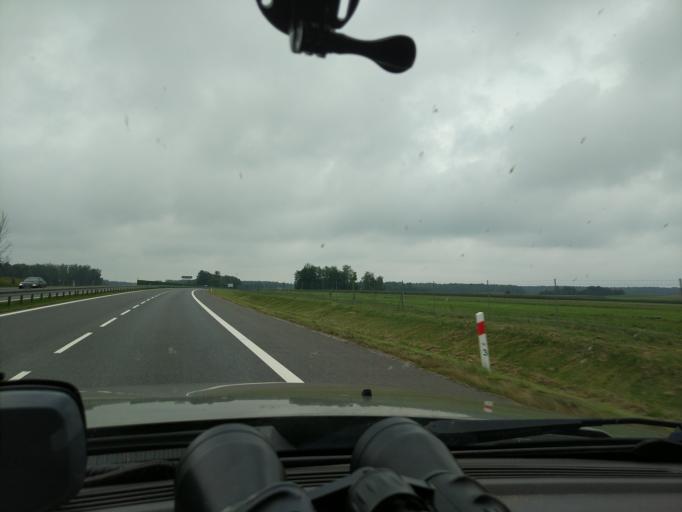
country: PL
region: Podlasie
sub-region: Powiat zambrowski
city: Zambrow
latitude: 53.0164
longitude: 22.3100
